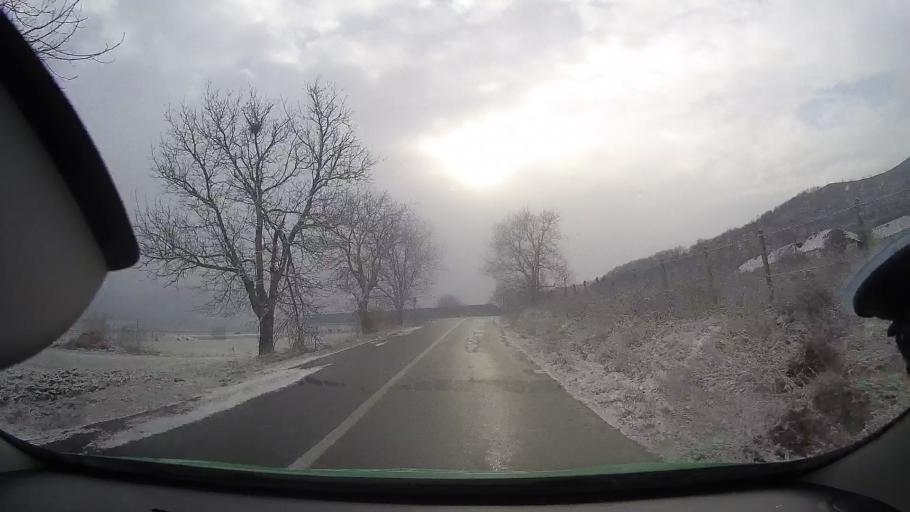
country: RO
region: Alba
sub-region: Comuna Rimetea
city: Rimetea
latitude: 46.4329
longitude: 23.5608
